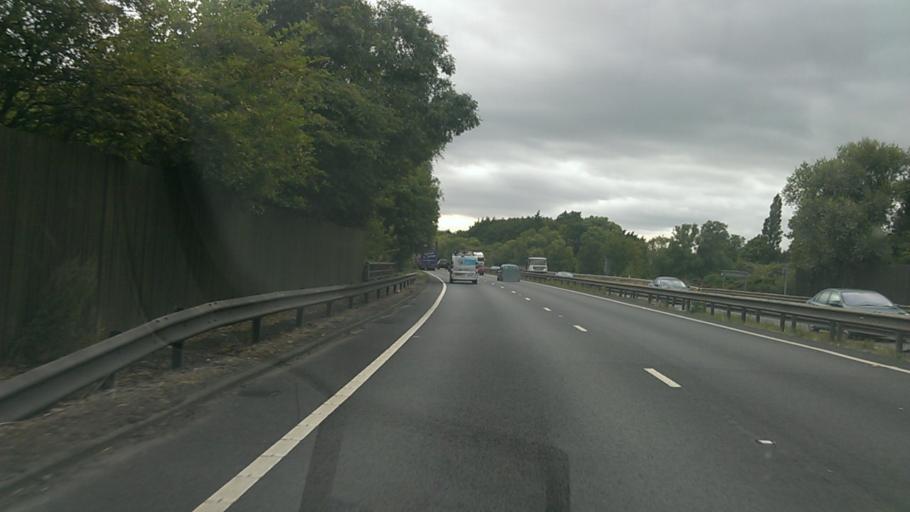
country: GB
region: England
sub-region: Cambridgeshire
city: Hemingford Grey
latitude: 52.2990
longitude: -0.0765
